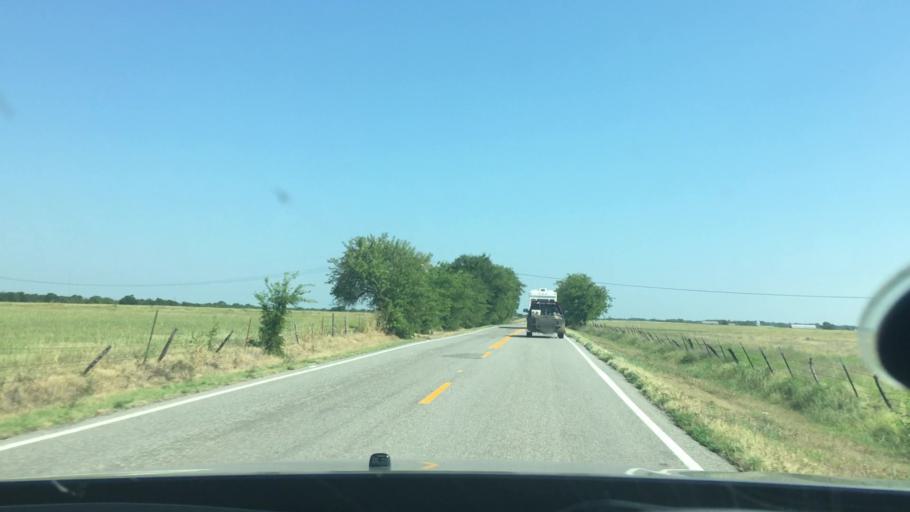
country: US
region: Oklahoma
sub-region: Johnston County
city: Tishomingo
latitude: 34.1630
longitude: -96.5082
